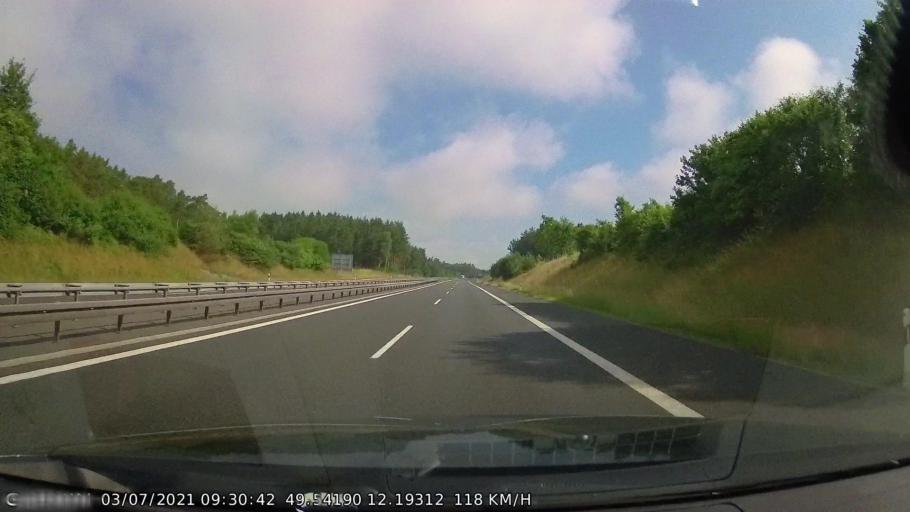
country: DE
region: Bavaria
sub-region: Upper Palatinate
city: Wernberg-Koblitz
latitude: 49.5420
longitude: 12.1931
